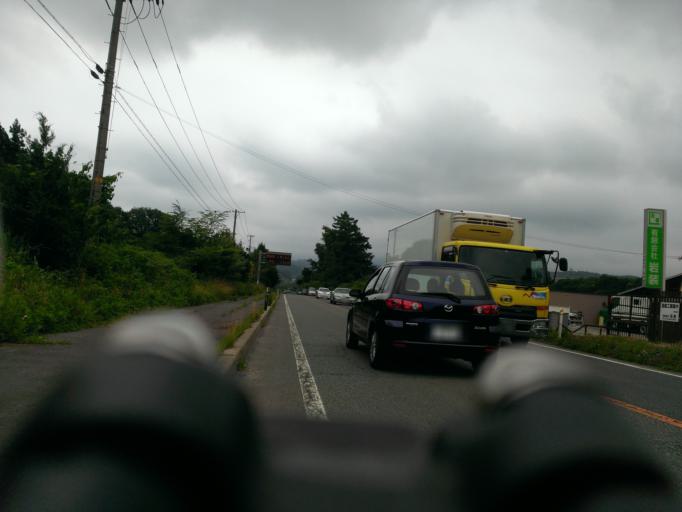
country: JP
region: Iwate
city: Morioka-shi
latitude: 39.8320
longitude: 141.1529
